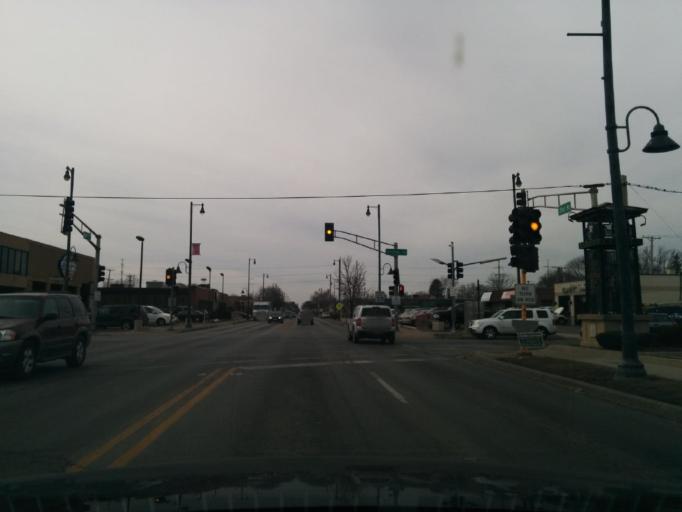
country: US
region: Illinois
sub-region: Cook County
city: La Grange Park
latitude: 41.8347
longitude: -87.8612
